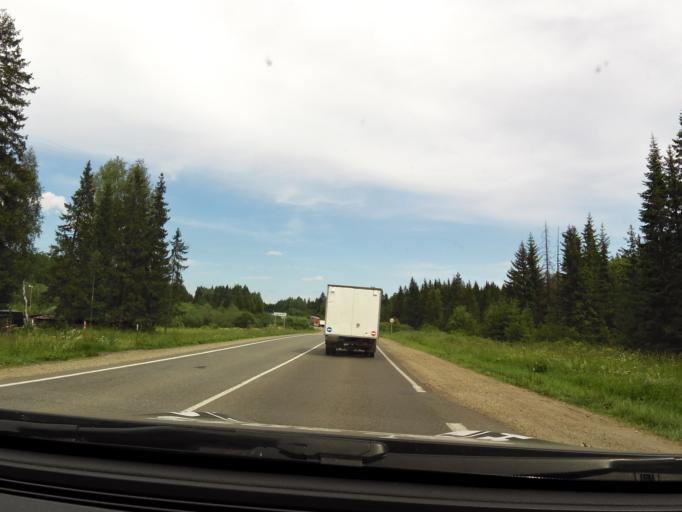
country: RU
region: Kirov
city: Vakhrushi
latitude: 58.6924
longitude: 50.0591
